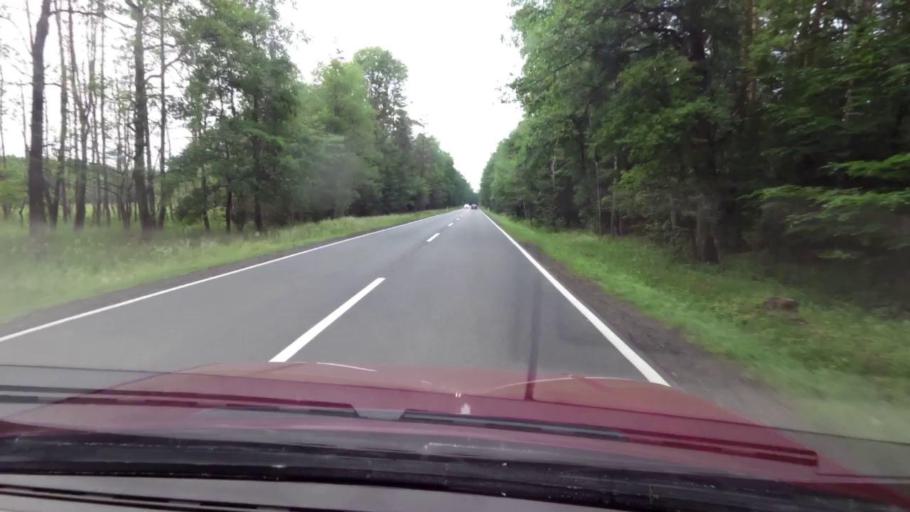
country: PL
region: Pomeranian Voivodeship
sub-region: Powiat bytowski
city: Trzebielino
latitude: 54.2253
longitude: 17.0872
